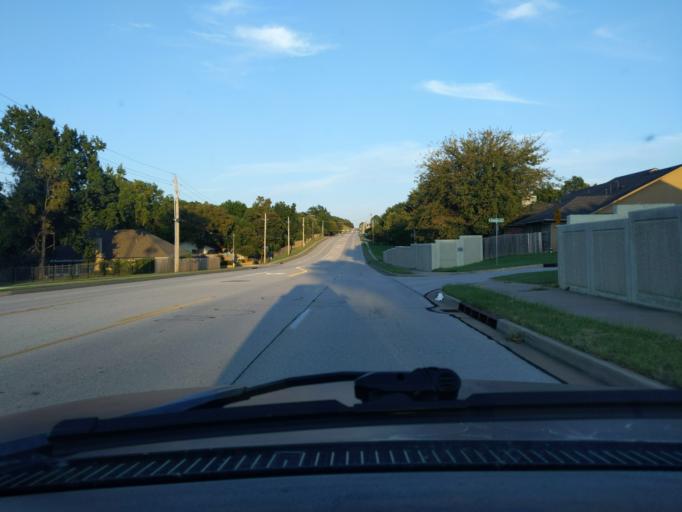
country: US
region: Oklahoma
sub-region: Tulsa County
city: Jenks
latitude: 36.0463
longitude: -95.9473
